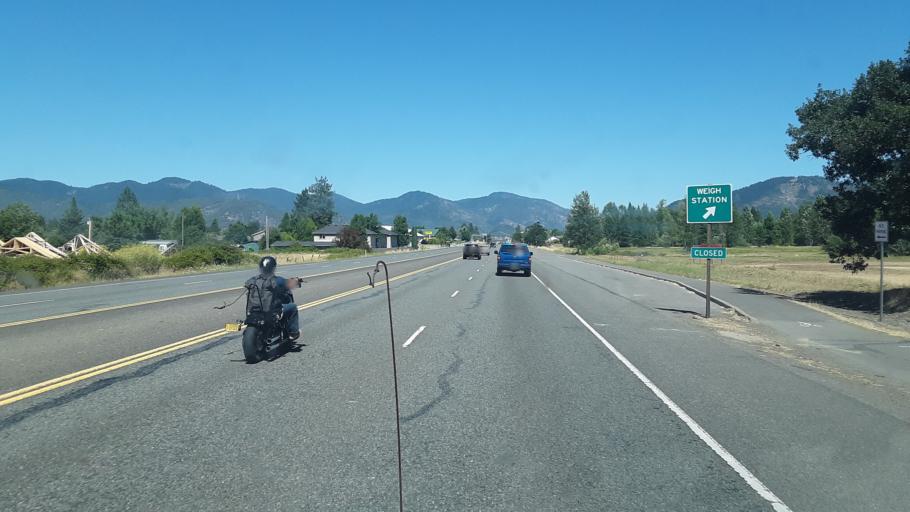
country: US
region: Oregon
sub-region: Josephine County
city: Redwood
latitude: 42.4191
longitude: -123.3635
